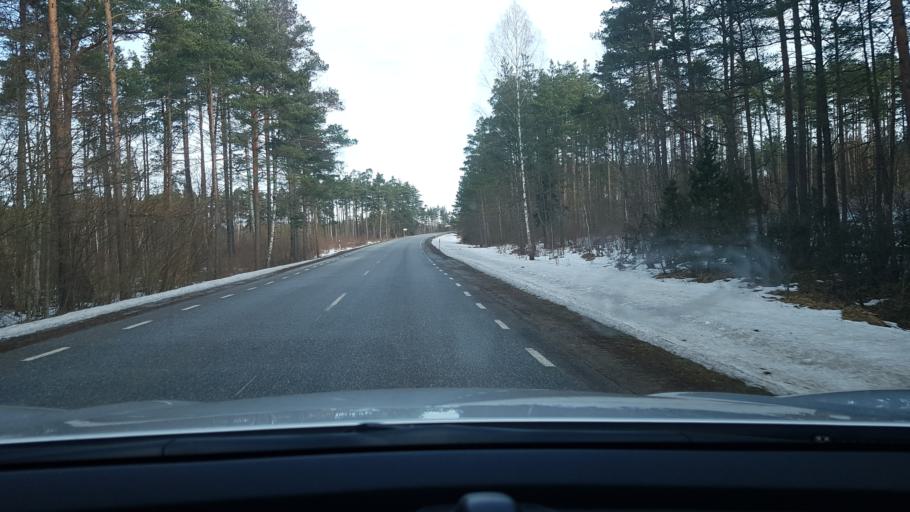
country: EE
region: Saare
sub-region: Kuressaare linn
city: Kuressaare
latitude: 58.4390
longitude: 22.7047
